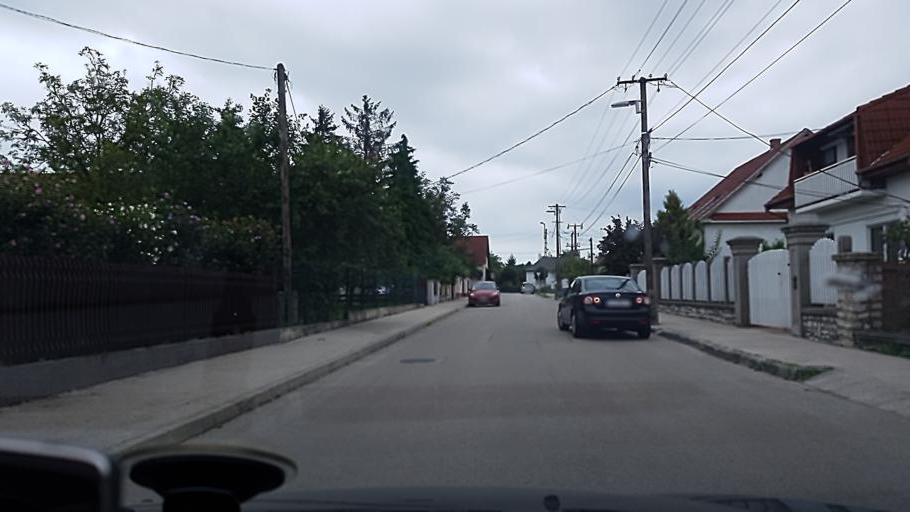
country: HU
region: Veszprem
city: Veszprem
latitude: 47.0938
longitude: 17.9202
